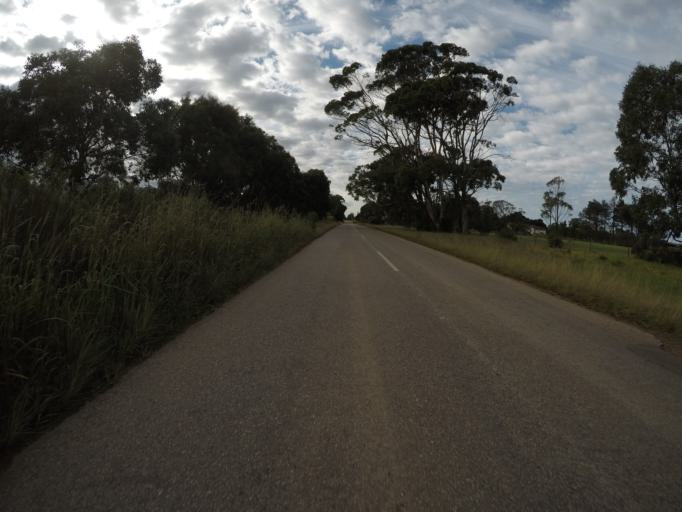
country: ZA
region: Eastern Cape
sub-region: Cacadu District Municipality
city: Kareedouw
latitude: -34.0441
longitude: 24.4331
